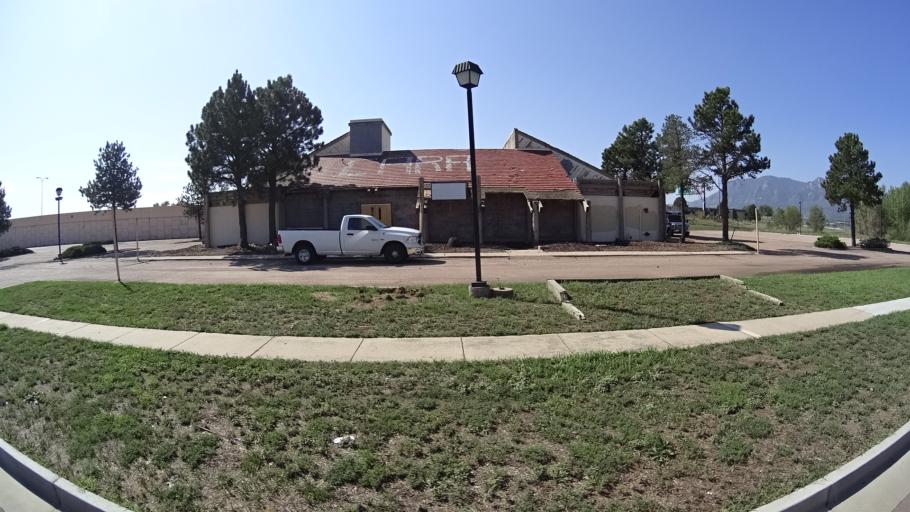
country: US
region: Colorado
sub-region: El Paso County
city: Colorado Springs
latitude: 38.8173
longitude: -104.7824
